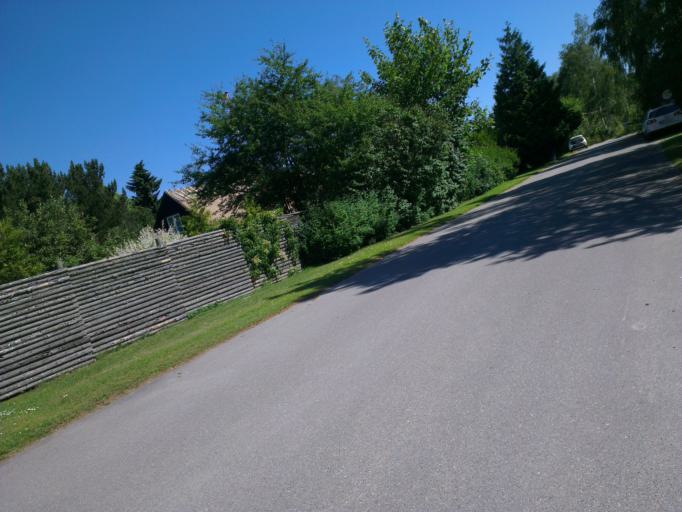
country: DK
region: Capital Region
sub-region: Frederikssund Kommune
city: Jaegerspris
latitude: 55.8175
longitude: 11.9434
